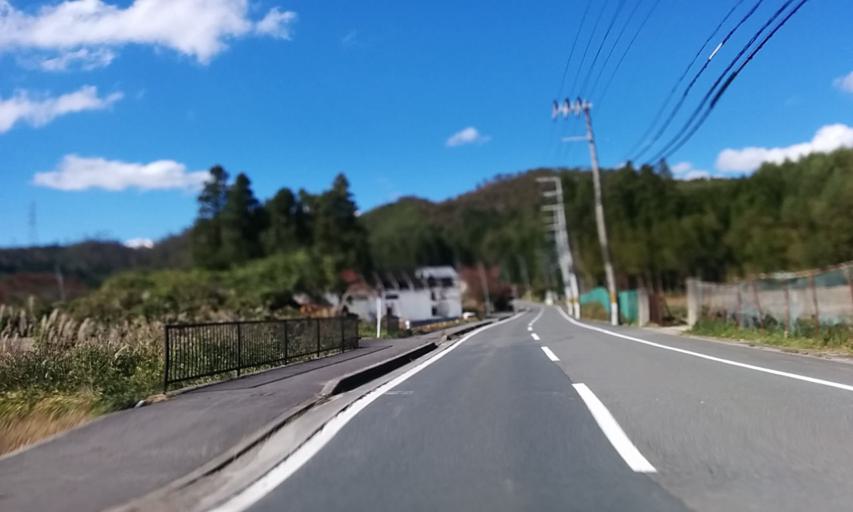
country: JP
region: Kyoto
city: Kameoka
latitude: 35.1981
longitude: 135.6324
